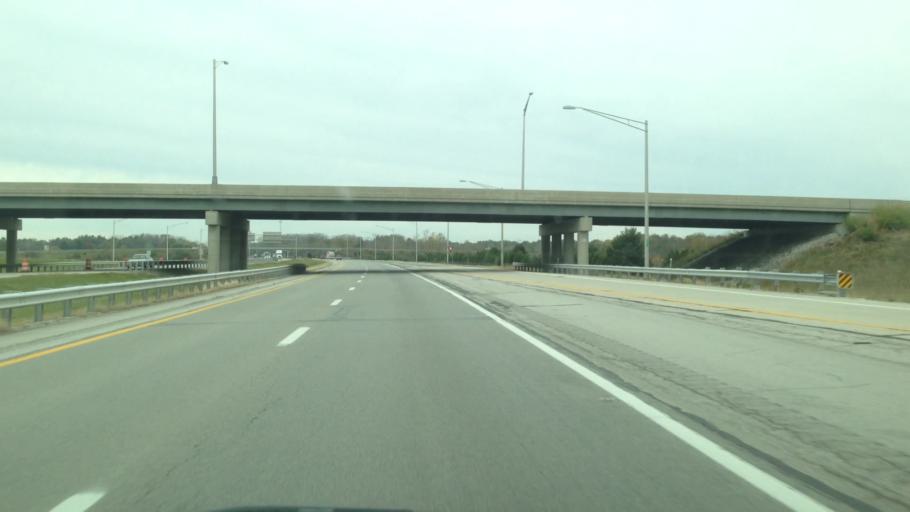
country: US
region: Ohio
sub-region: Fulton County
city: Burlington
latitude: 41.5919
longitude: -84.3191
